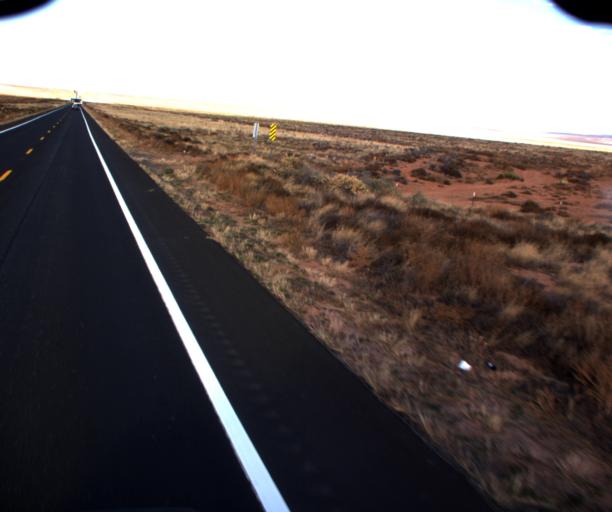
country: US
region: Arizona
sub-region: Apache County
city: Lukachukai
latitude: 36.9618
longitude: -109.4104
